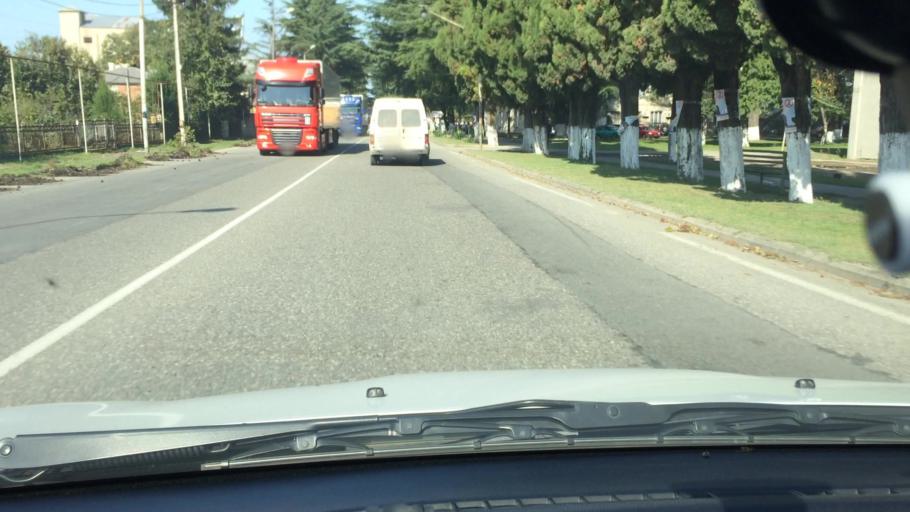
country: GE
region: Guria
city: Lanchkhuti
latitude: 42.0857
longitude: 42.0400
